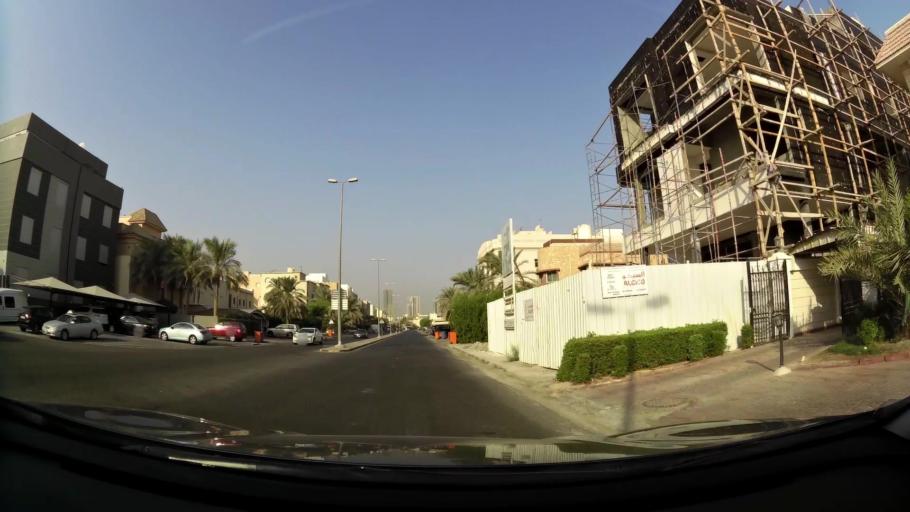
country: KW
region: Al Asimah
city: Ad Dasmah
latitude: 29.3628
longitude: 48.0050
